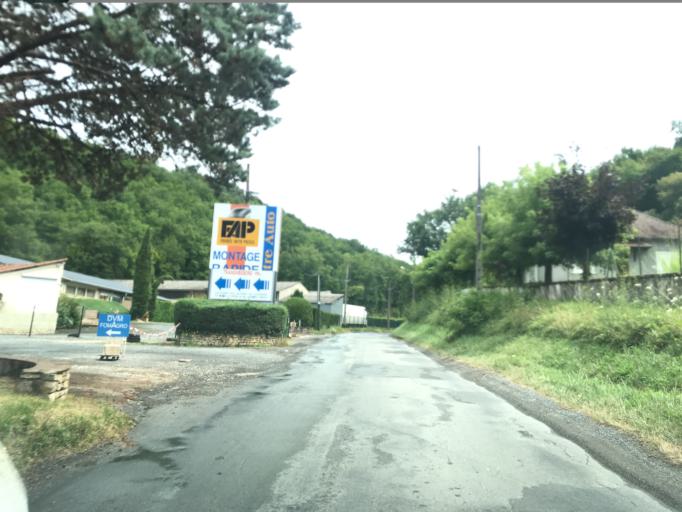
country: FR
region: Aquitaine
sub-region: Departement de la Dordogne
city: Chancelade
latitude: 45.1811
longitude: 0.6682
